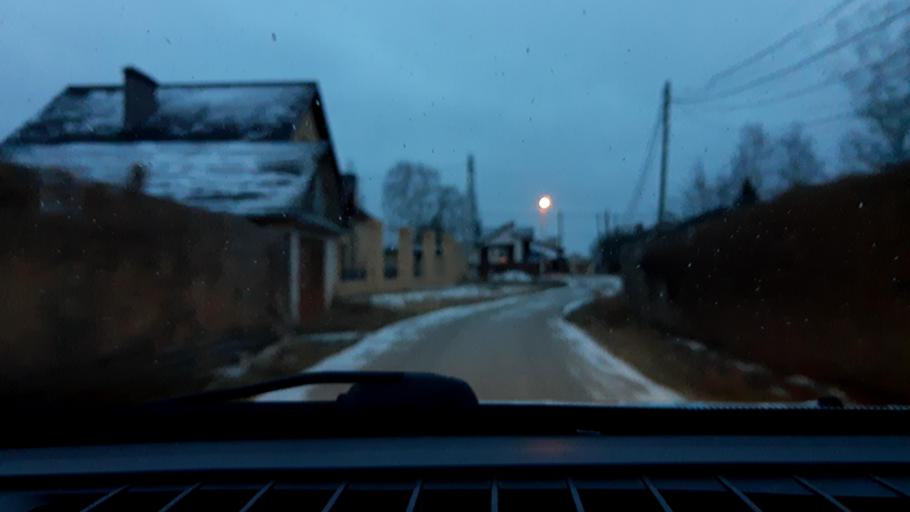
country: RU
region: Nizjnij Novgorod
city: Gorbatovka
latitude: 56.3870
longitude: 43.7518
